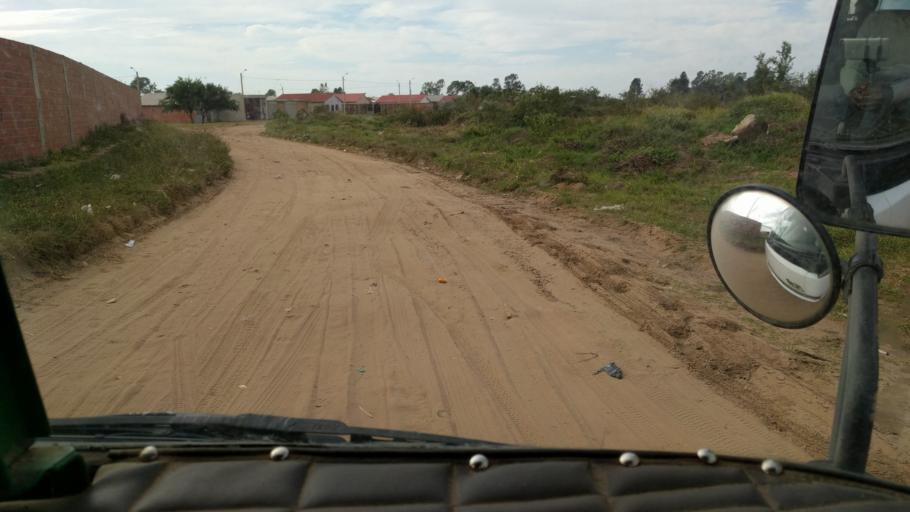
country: BO
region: Santa Cruz
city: Santa Cruz de la Sierra
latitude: -17.6871
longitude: -63.1439
